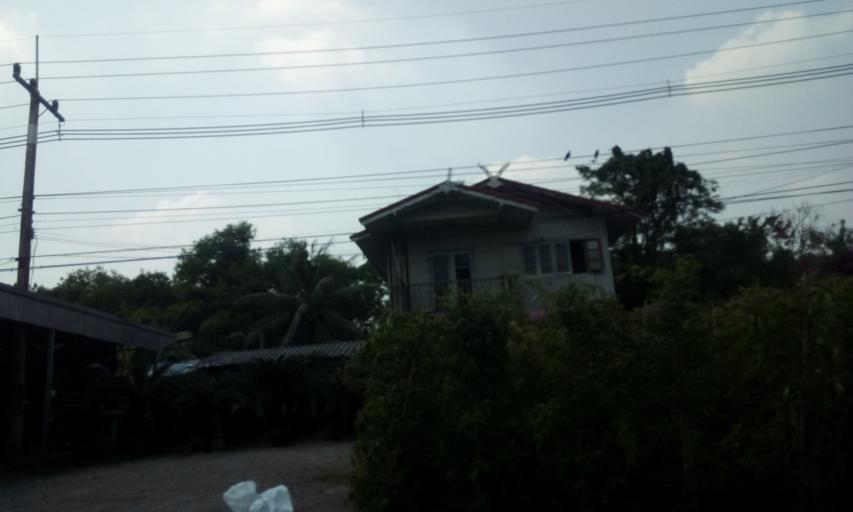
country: TH
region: Nakhon Nayok
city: Ongkharak
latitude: 14.1244
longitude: 100.9429
